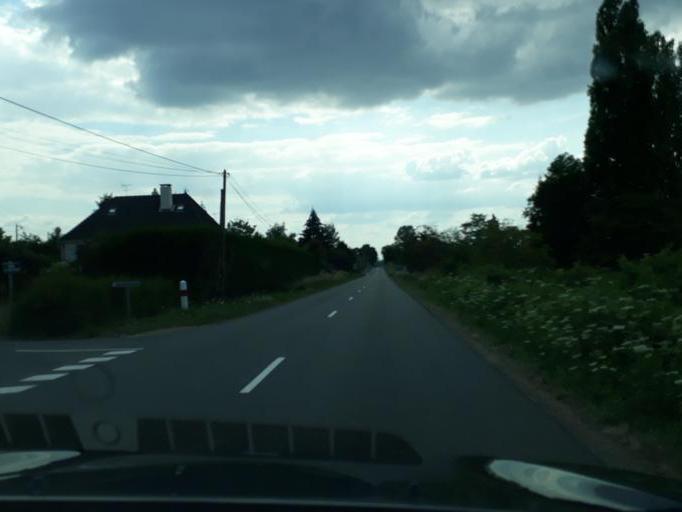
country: FR
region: Centre
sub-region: Departement du Cher
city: Cours-les-Barres
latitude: 46.9816
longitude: 2.9858
